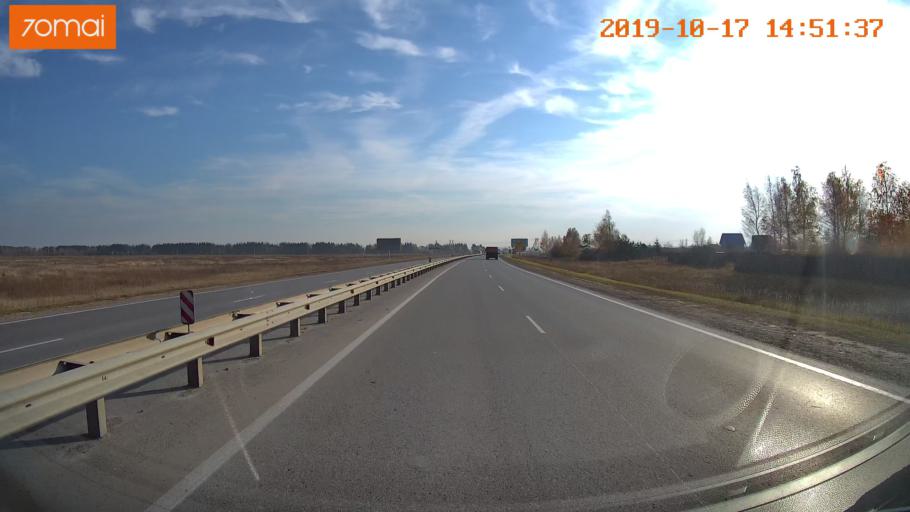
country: RU
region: Rjazan
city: Polyany
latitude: 54.7172
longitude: 39.8487
